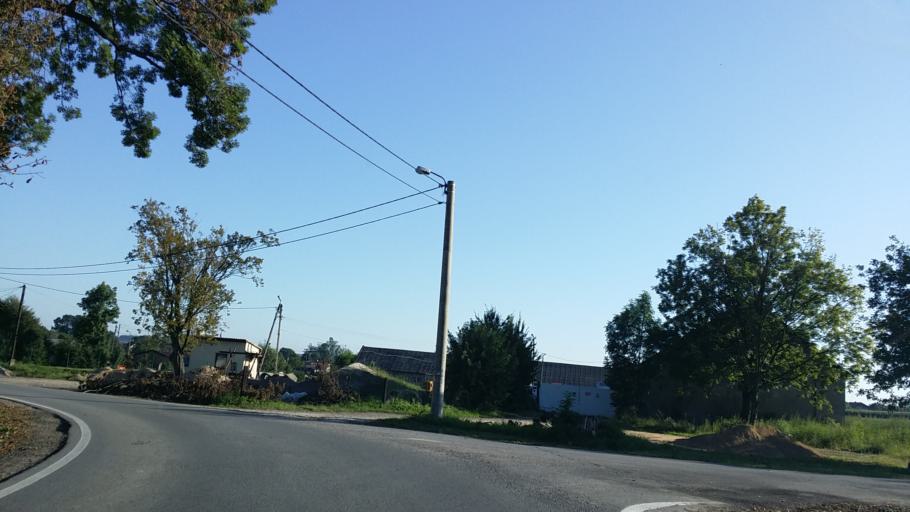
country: PL
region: Lesser Poland Voivodeship
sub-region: Powiat wadowicki
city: Spytkowice
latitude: 50.0035
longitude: 19.5125
